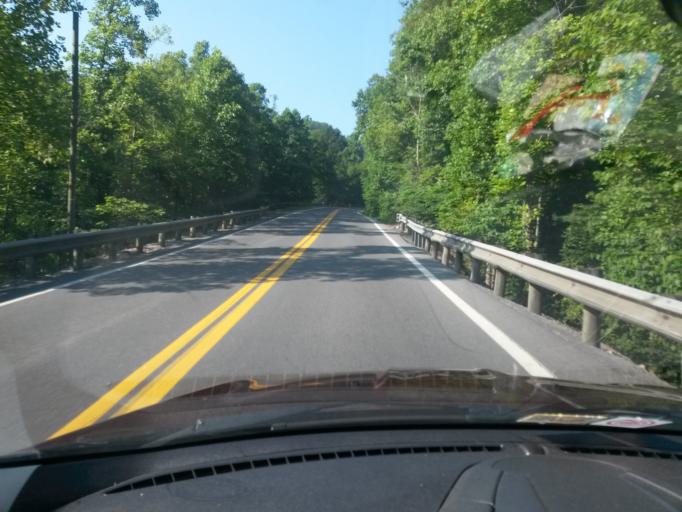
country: US
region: West Virginia
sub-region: Wyoming County
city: Pineville
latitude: 37.5583
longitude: -81.5424
